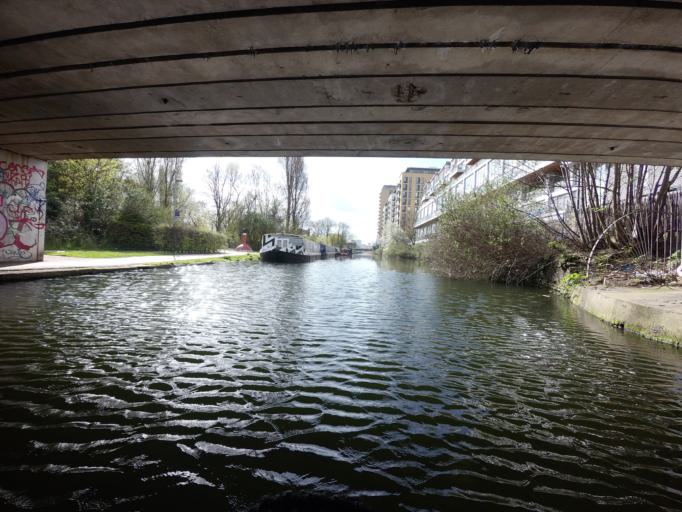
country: GB
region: England
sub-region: Greater London
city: Bethnal Green
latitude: 51.5304
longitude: -0.0421
